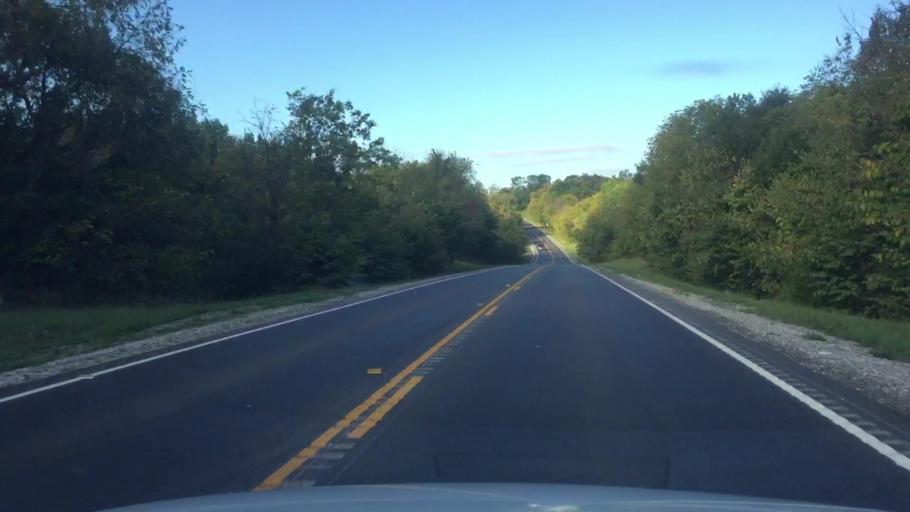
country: US
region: Missouri
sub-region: Howard County
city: New Franklin
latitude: 38.9974
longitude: -92.5935
